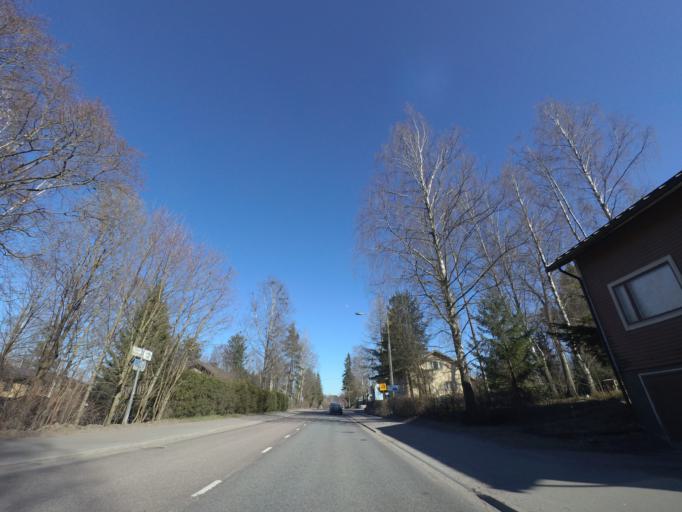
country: FI
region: Uusimaa
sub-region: Helsinki
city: Vantaa
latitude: 60.2516
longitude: 25.0831
